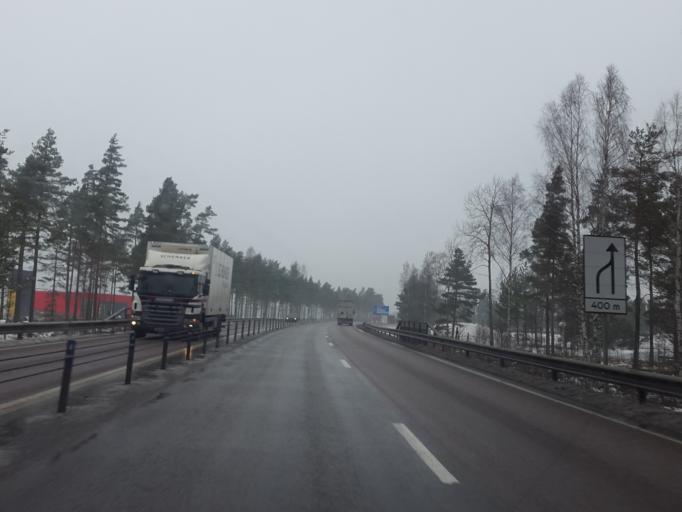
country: SE
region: Joenkoeping
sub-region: Jonkopings Kommun
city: Jonkoping
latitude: 57.7675
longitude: 14.0916
